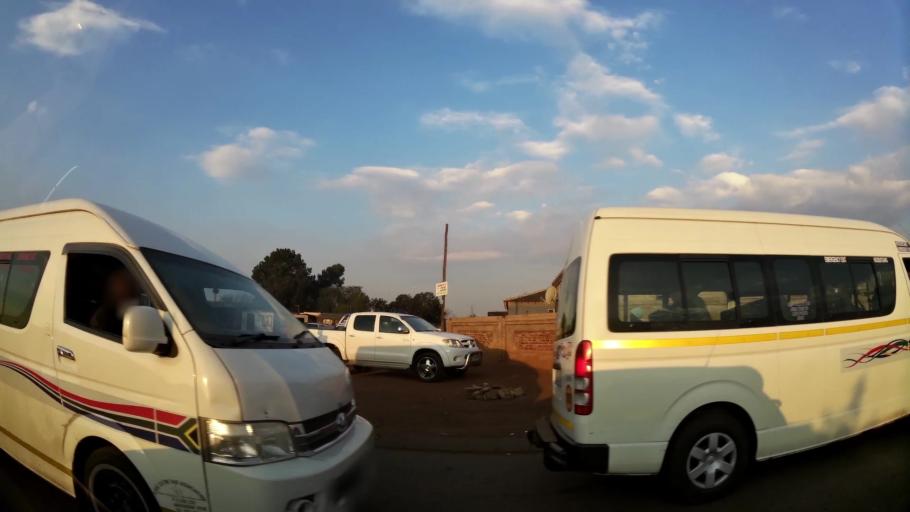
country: ZA
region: Gauteng
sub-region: City of Johannesburg Metropolitan Municipality
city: Orange Farm
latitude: -26.5537
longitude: 27.8632
